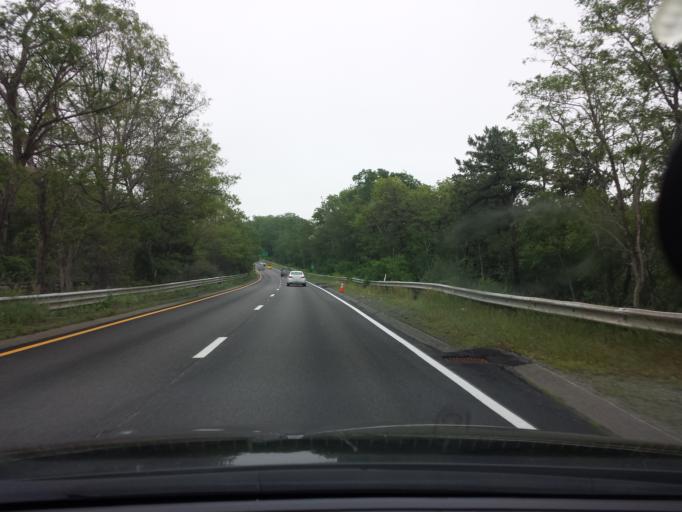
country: US
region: Massachusetts
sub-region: Barnstable County
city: Sandwich
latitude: 41.7468
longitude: -70.5131
